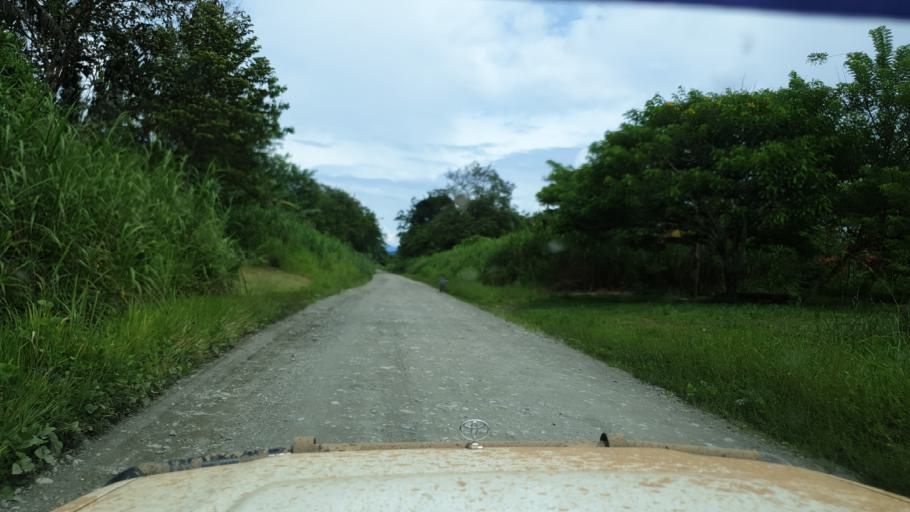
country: PG
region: Northern Province
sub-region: Sohe
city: Kokoda
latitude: -8.8903
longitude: 147.7476
